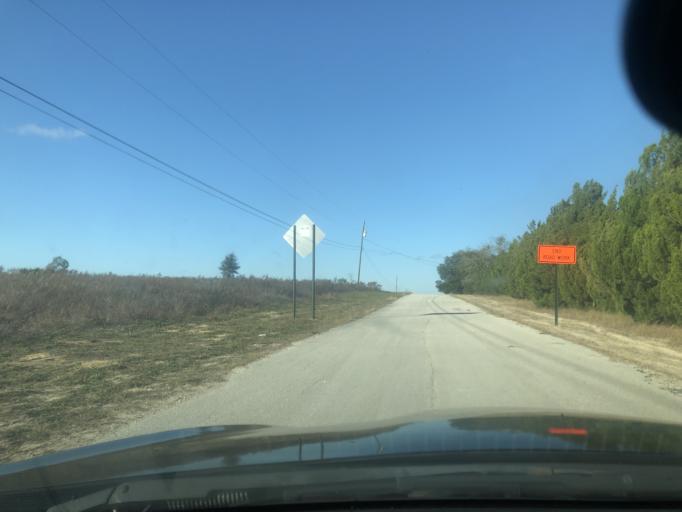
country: US
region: Florida
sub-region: Citrus County
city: Sugarmill Woods
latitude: 28.7651
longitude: -82.4954
